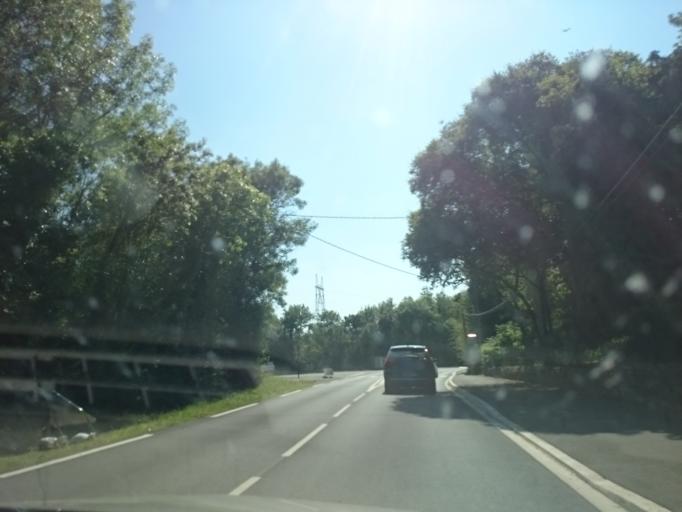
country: FR
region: Pays de la Loire
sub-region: Departement de la Loire-Atlantique
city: Le Pellerin
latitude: 47.2103
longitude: -1.7428
